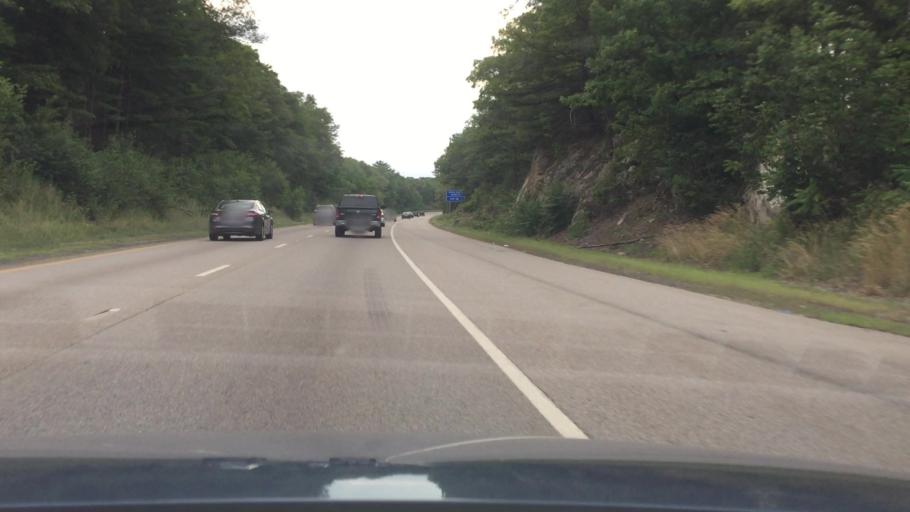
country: US
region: Massachusetts
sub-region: Norfolk County
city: Weymouth
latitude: 42.1894
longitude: -70.9396
